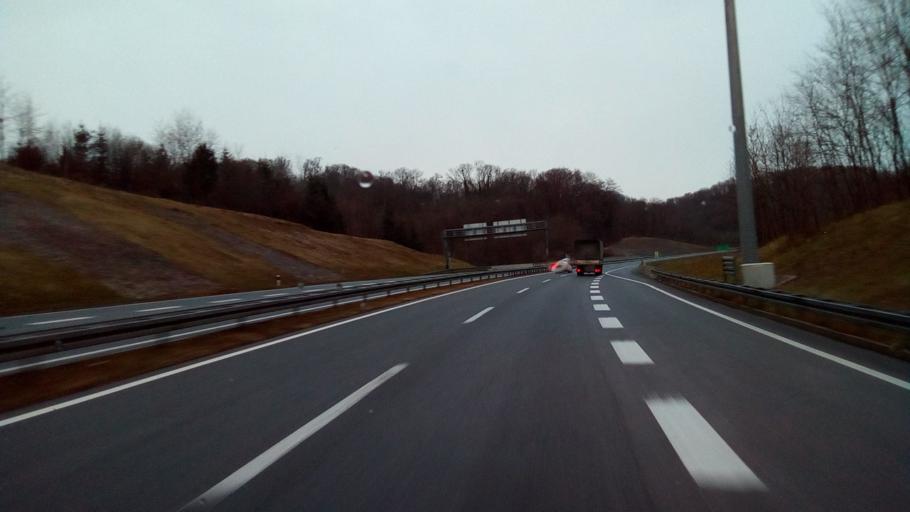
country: HR
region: Varazdinska
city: Ljubescica
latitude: 46.2108
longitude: 16.4062
